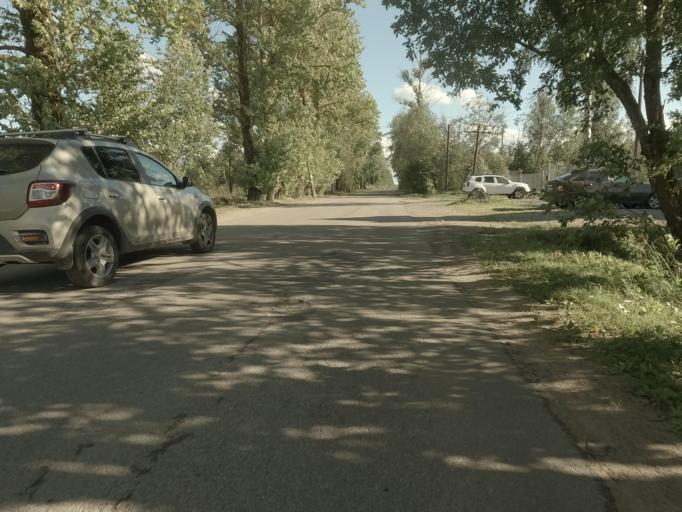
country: RU
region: Leningrad
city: Imeni Morozova
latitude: 59.9690
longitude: 31.0280
